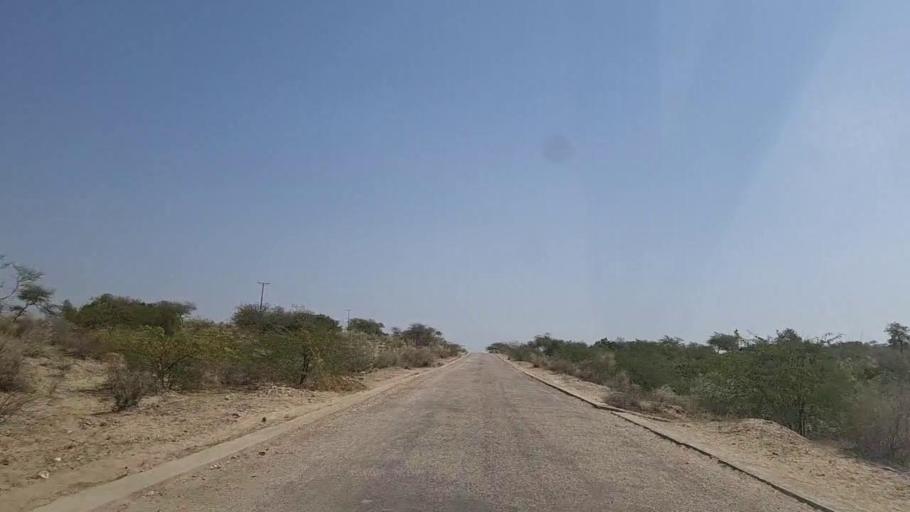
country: PK
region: Sindh
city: Diplo
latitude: 24.5139
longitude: 69.3877
